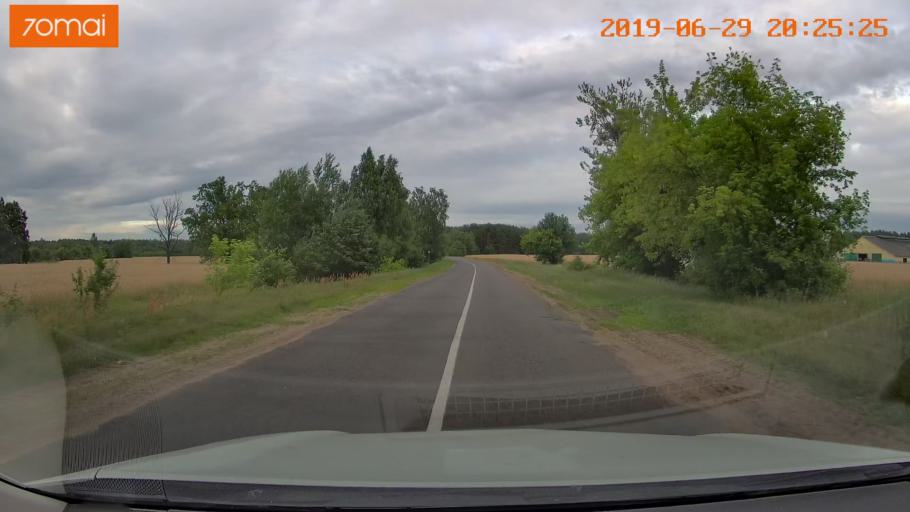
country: BY
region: Brest
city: Asnyezhytsy
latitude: 52.4571
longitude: 26.2801
